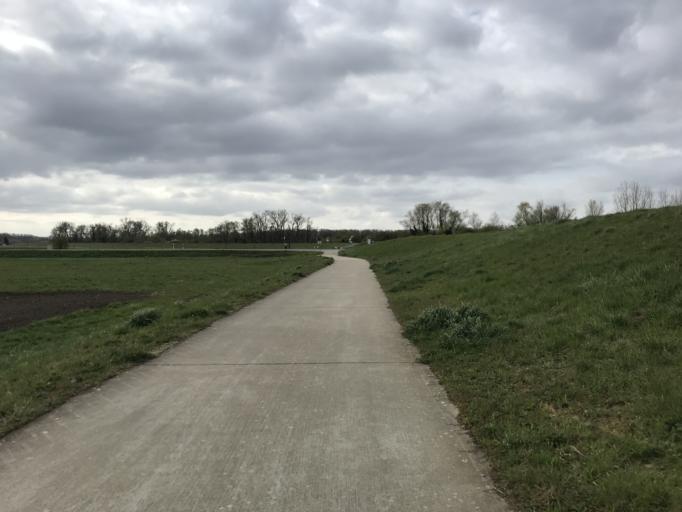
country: DE
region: Rheinland-Pfalz
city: Oppenheim
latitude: 49.8699
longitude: 8.3691
